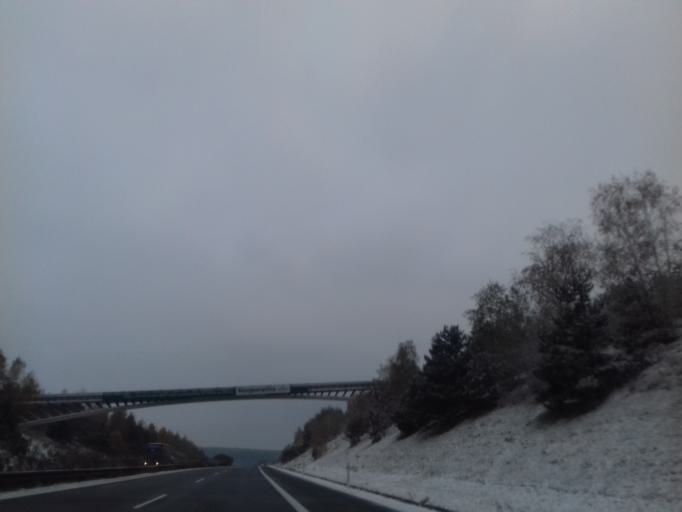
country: CZ
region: Plzensky
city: Zbiroh
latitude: 49.8216
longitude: 13.7701
